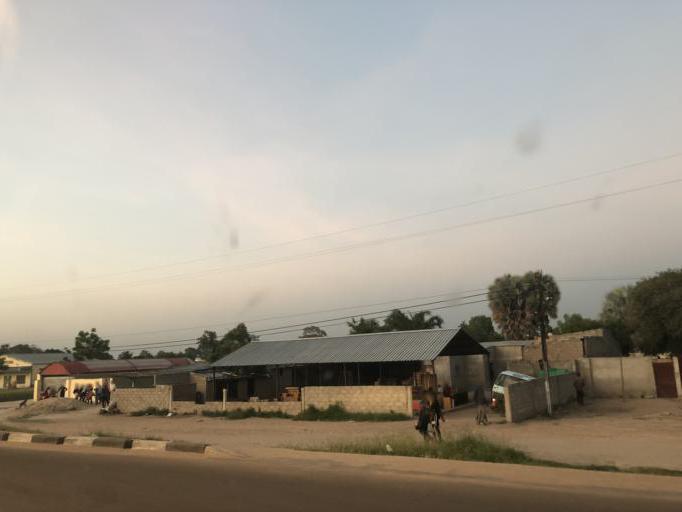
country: AO
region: Cunene
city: Ondjiva
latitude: -17.0687
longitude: 15.7102
